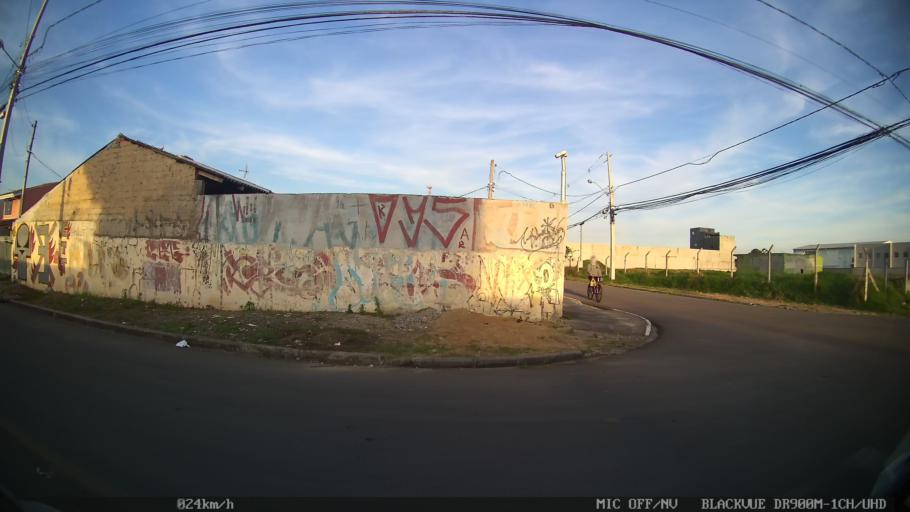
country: BR
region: Parana
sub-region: Pinhais
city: Pinhais
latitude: -25.4465
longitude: -49.1692
